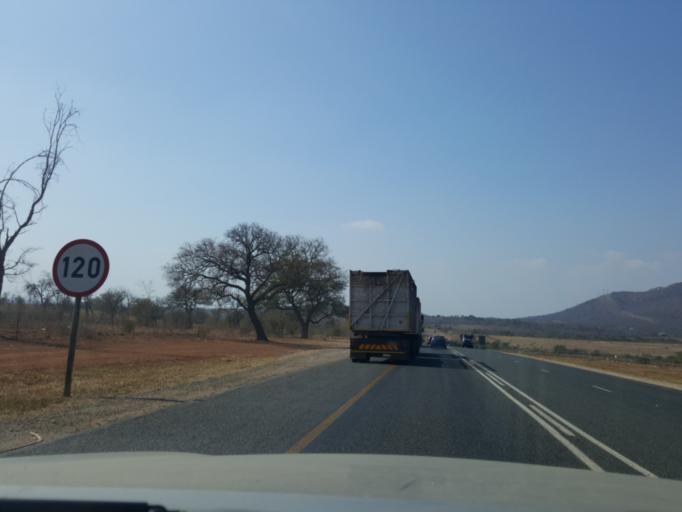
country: ZA
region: Mpumalanga
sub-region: Ehlanzeni District
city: Komatipoort
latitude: -25.4755
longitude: 31.5721
